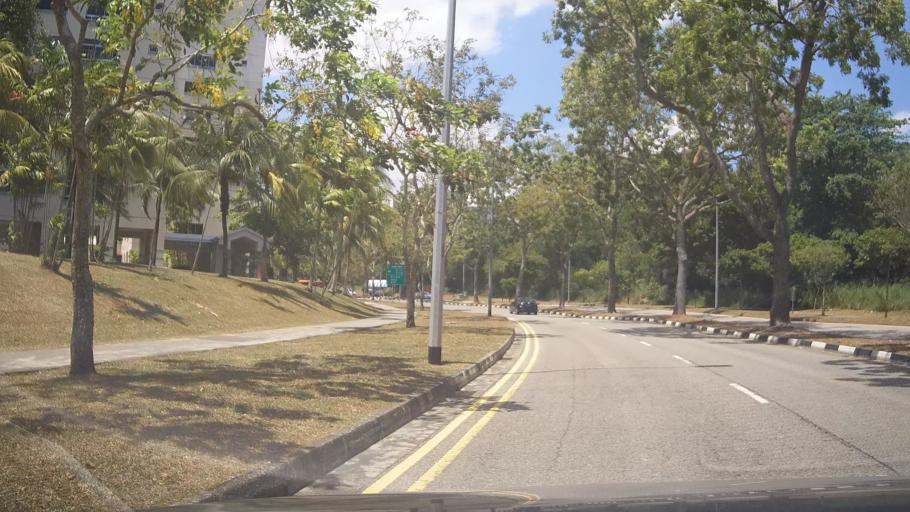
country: MY
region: Johor
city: Kampung Pasir Gudang Baru
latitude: 1.3741
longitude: 103.9635
